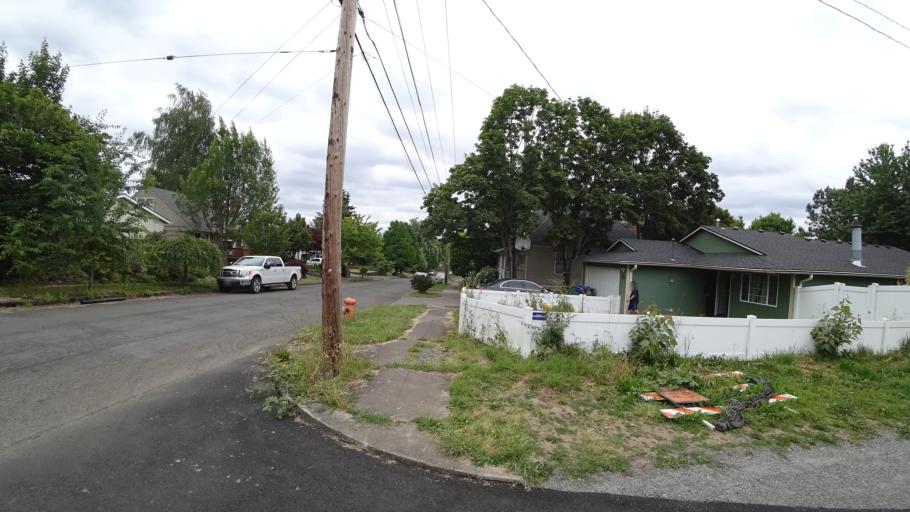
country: US
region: Oregon
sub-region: Multnomah County
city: Lents
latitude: 45.5114
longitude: -122.5837
